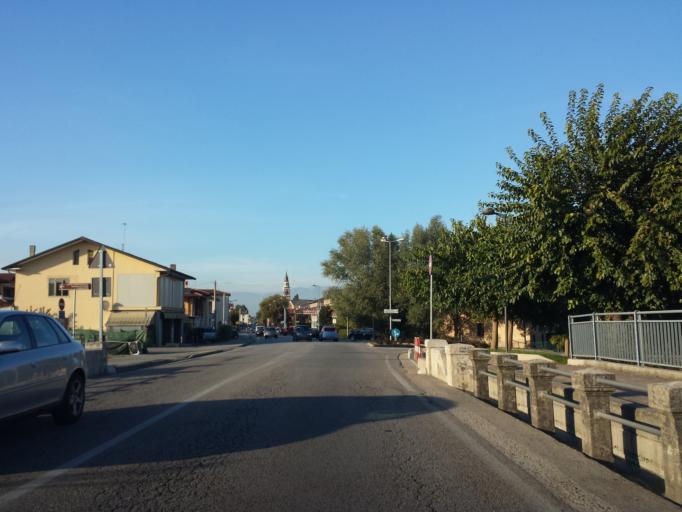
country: IT
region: Veneto
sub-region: Provincia di Vicenza
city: Motta
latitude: 45.5945
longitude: 11.4969
